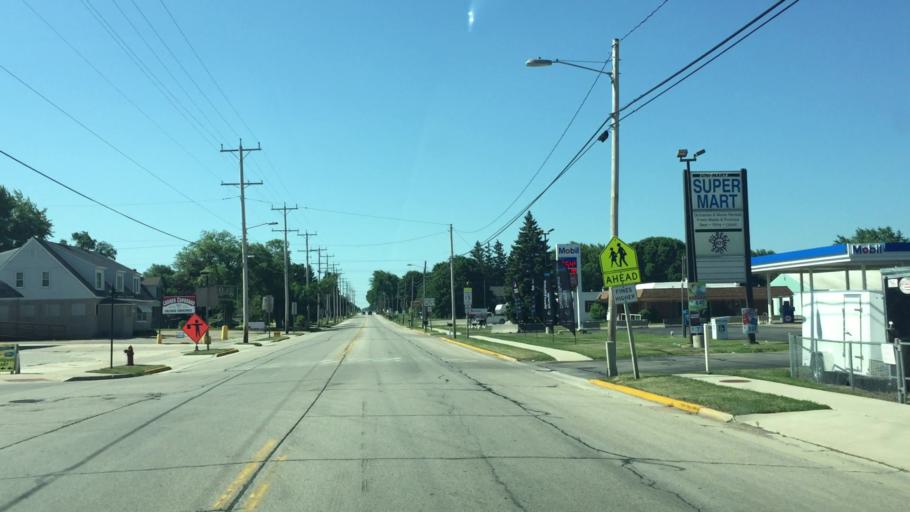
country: US
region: Wisconsin
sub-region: Calumet County
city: Hilbert
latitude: 44.1395
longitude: -88.1641
